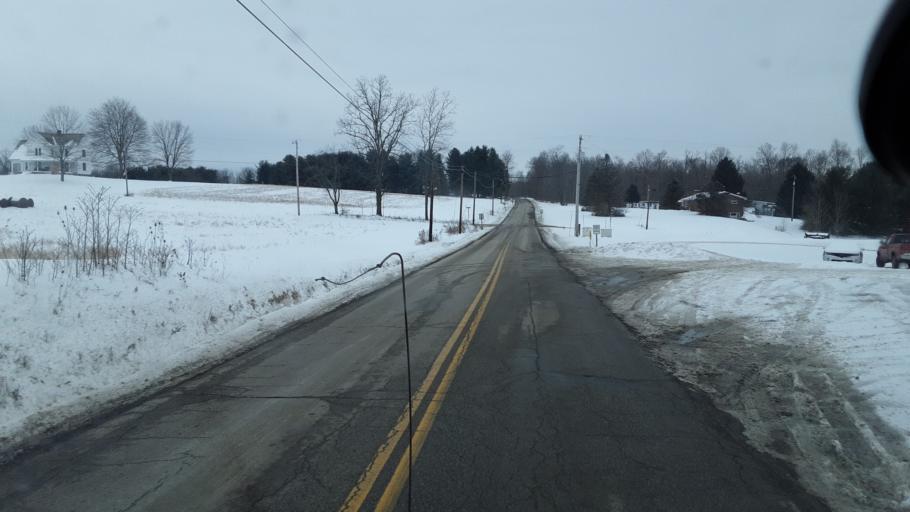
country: US
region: Ohio
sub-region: Perry County
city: Somerset
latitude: 39.9238
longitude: -82.2243
